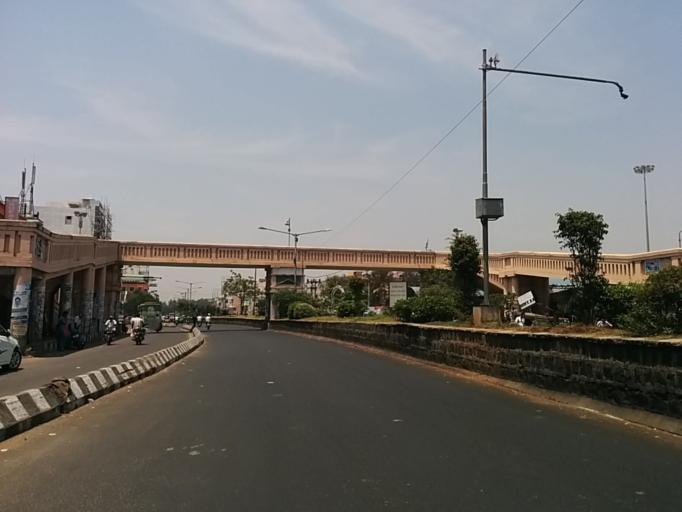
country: IN
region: Pondicherry
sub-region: Puducherry
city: Puducherry
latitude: 11.9317
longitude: 79.8166
